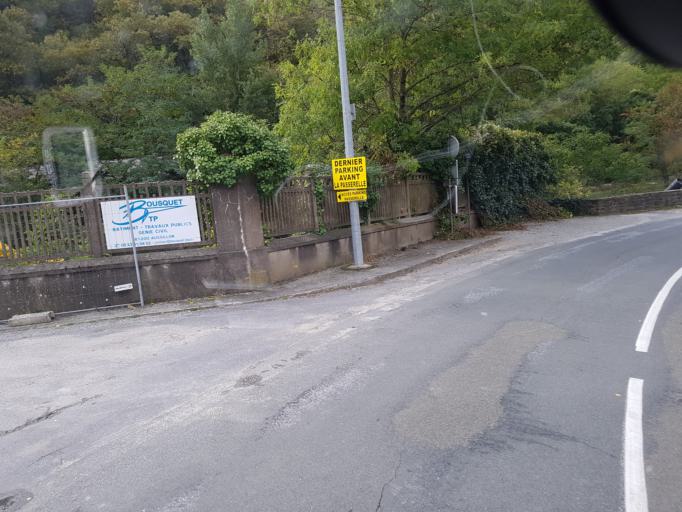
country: FR
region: Midi-Pyrenees
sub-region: Departement du Tarn
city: Mazamet
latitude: 43.4806
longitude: 2.3759
